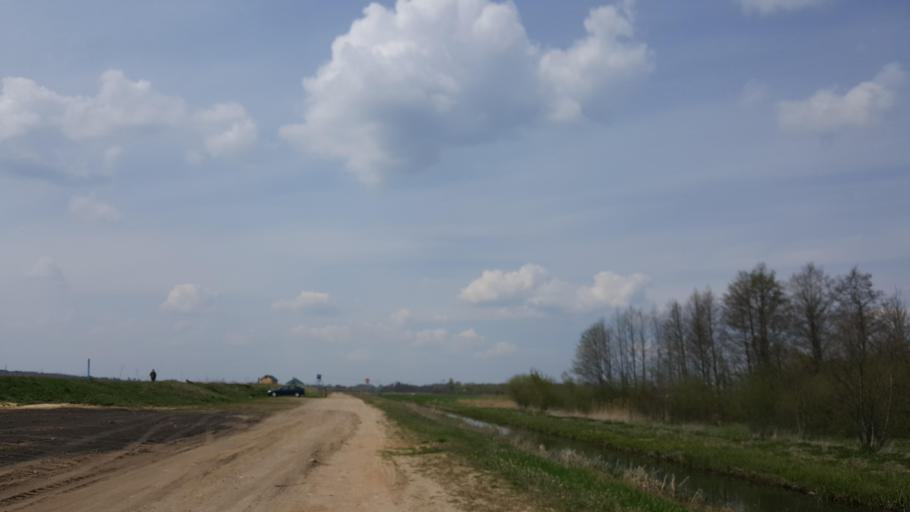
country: BY
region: Brest
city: Zhabinka
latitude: 52.2004
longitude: 23.9901
